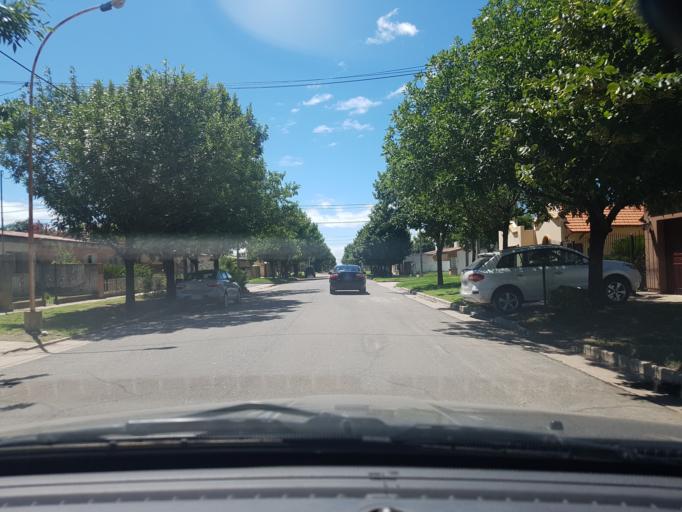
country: AR
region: Cordoba
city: Las Perdices
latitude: -32.7574
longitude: -63.7781
